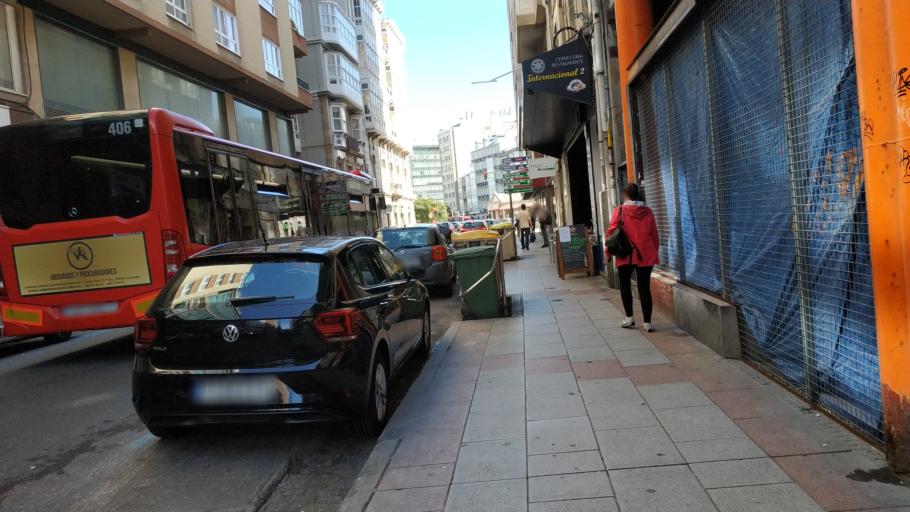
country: ES
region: Galicia
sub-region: Provincia da Coruna
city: A Coruna
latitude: 43.3678
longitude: -8.4091
